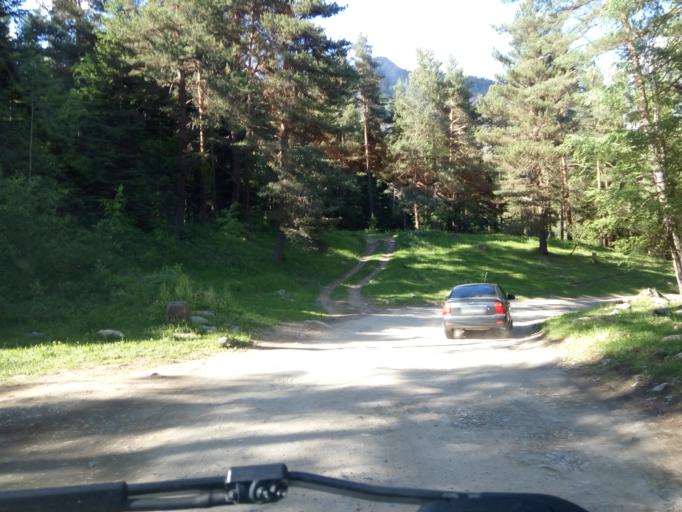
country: RU
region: Karachayevo-Cherkesiya
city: Nizhniy Arkhyz
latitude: 43.5304
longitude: 41.2360
